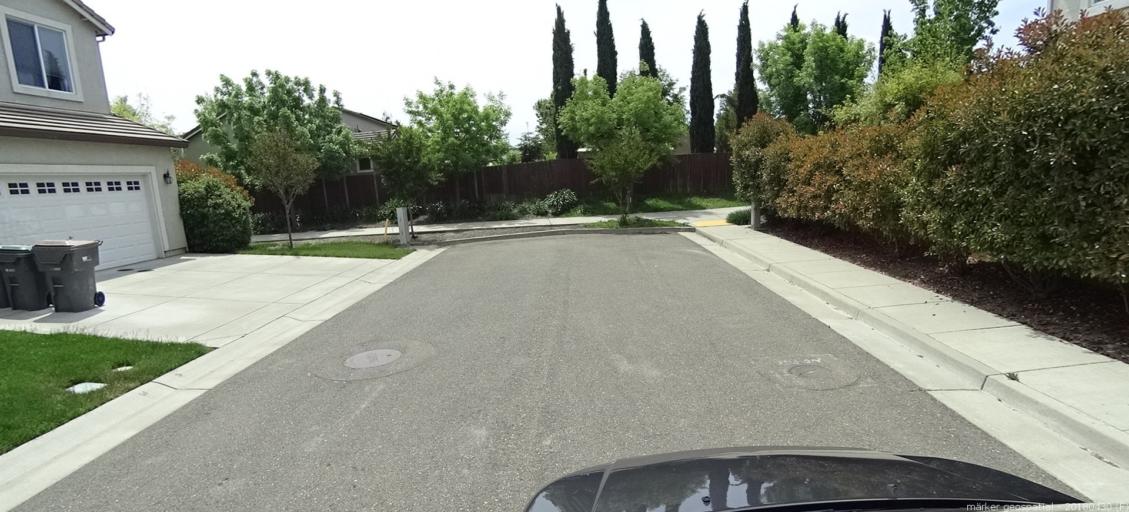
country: US
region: California
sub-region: Yolo County
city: West Sacramento
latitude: 38.5450
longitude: -121.5329
